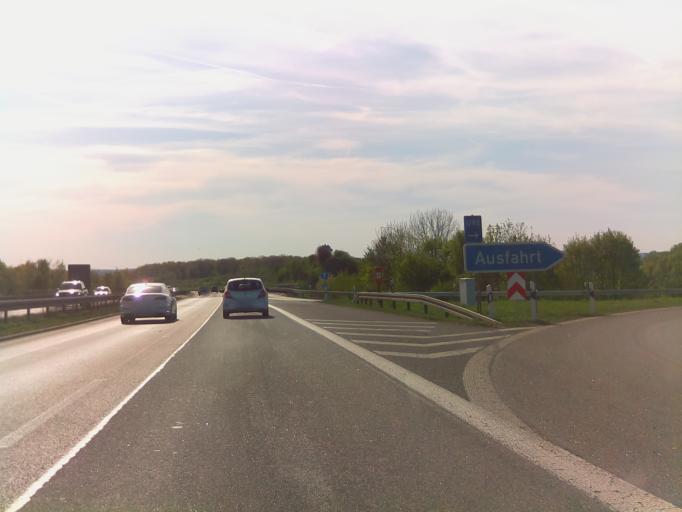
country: DE
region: Bavaria
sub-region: Regierungsbezirk Unterfranken
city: Sennfeld
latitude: 50.0301
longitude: 10.2662
